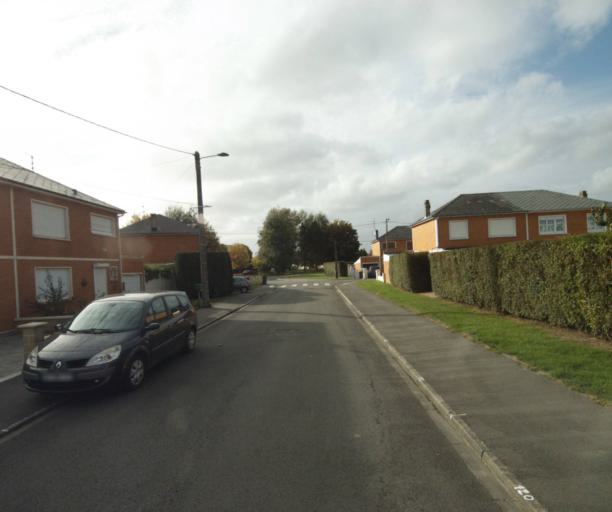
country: FR
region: Nord-Pas-de-Calais
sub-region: Departement du Nord
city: La Bassee
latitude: 50.5391
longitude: 2.8039
